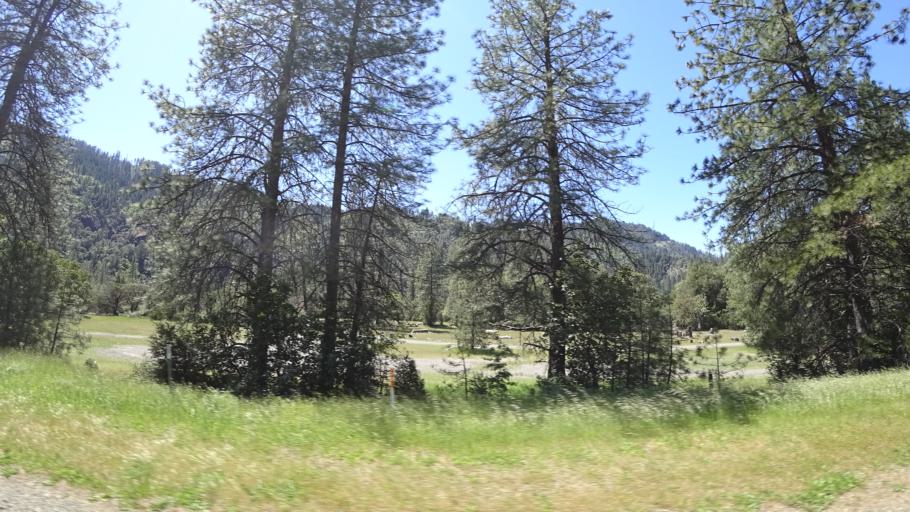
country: US
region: California
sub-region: Trinity County
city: Hayfork
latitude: 40.7756
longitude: -123.3326
